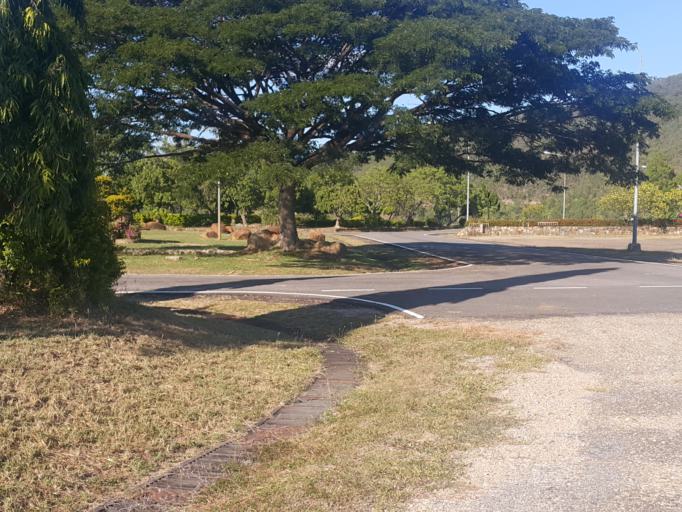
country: TH
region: Chiang Mai
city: San Sai
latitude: 18.9239
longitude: 99.1226
